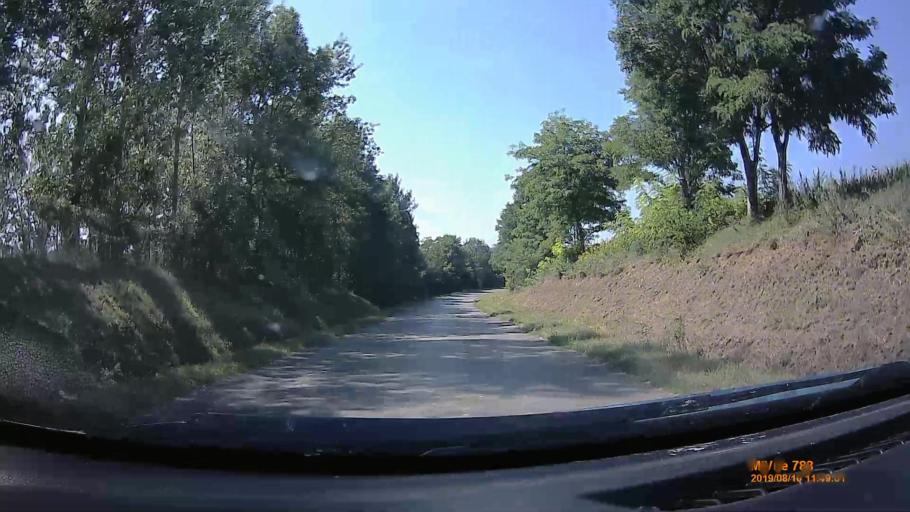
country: HU
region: Somogy
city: Somogyvar
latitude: 46.5000
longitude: 17.7335
